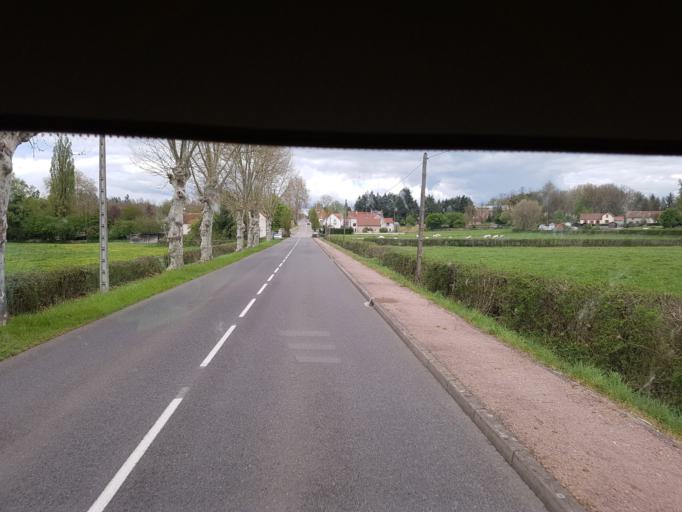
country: FR
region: Bourgogne
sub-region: Departement de Saone-et-Loire
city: Genelard
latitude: 46.5745
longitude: 4.2355
